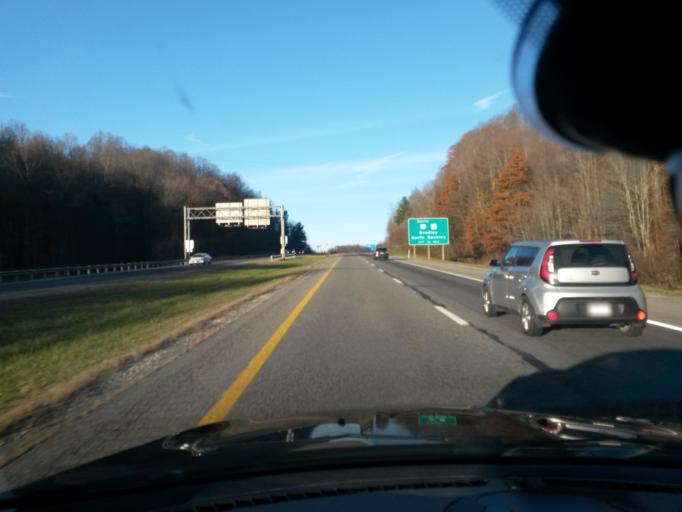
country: US
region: West Virginia
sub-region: Raleigh County
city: Prosperity
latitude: 37.8433
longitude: -81.2095
